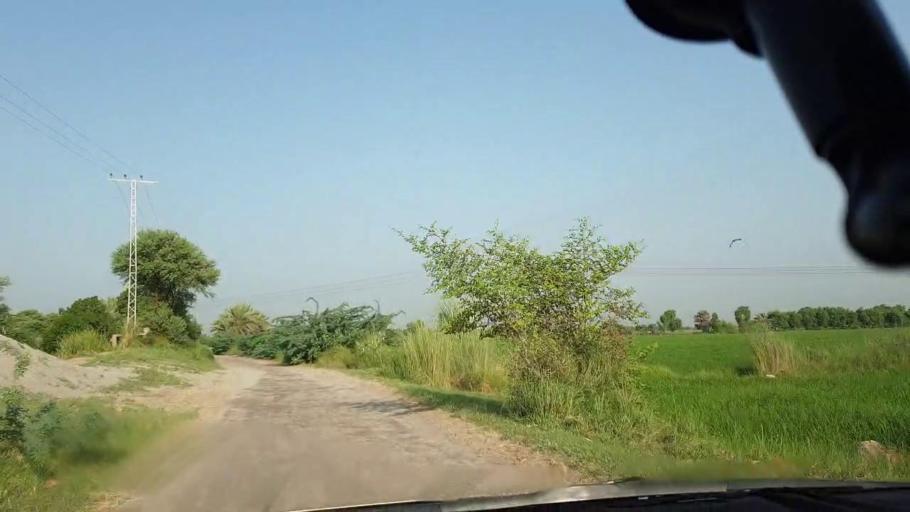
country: PK
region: Sindh
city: Larkana
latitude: 27.6205
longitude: 68.2097
